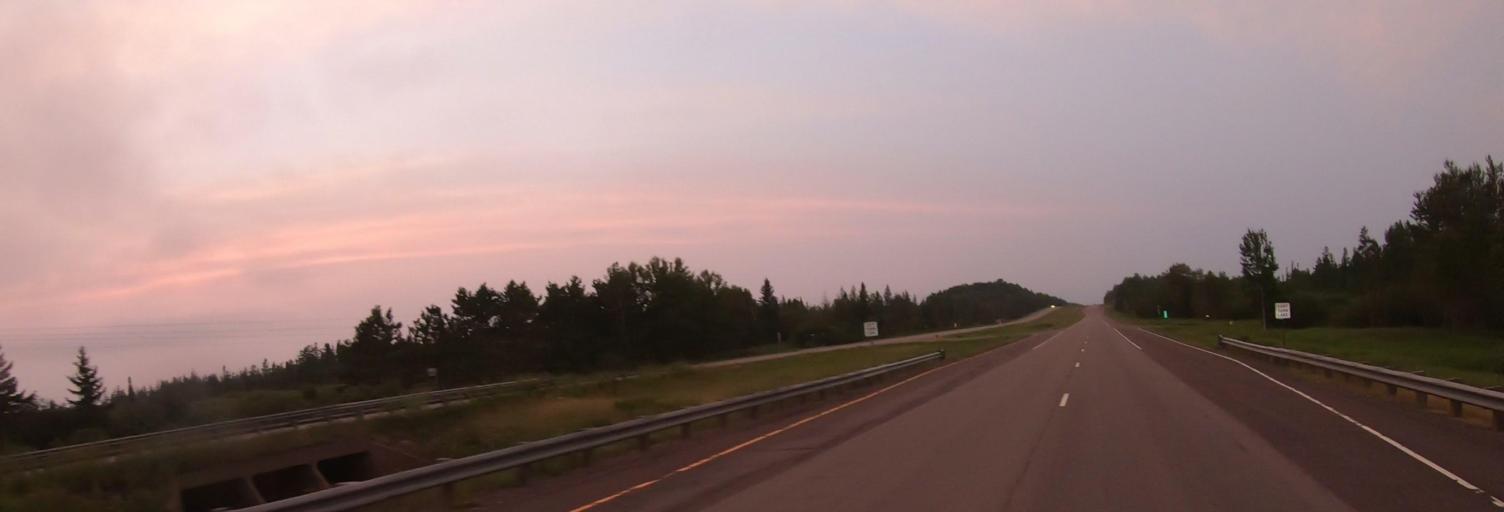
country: US
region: Minnesota
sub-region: Carlton County
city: Cloquet
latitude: 46.9952
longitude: -92.4708
